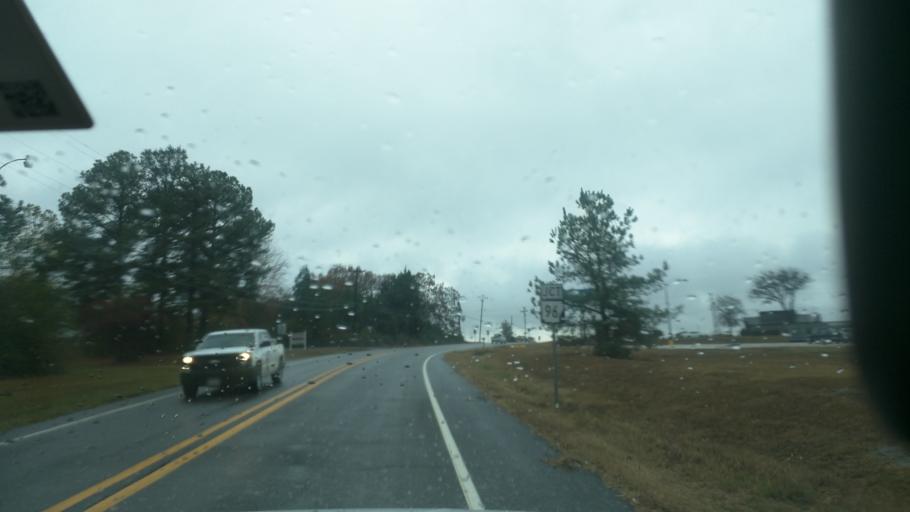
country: US
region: Arkansas
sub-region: Franklin County
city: Ozark
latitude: 35.5027
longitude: -93.8450
